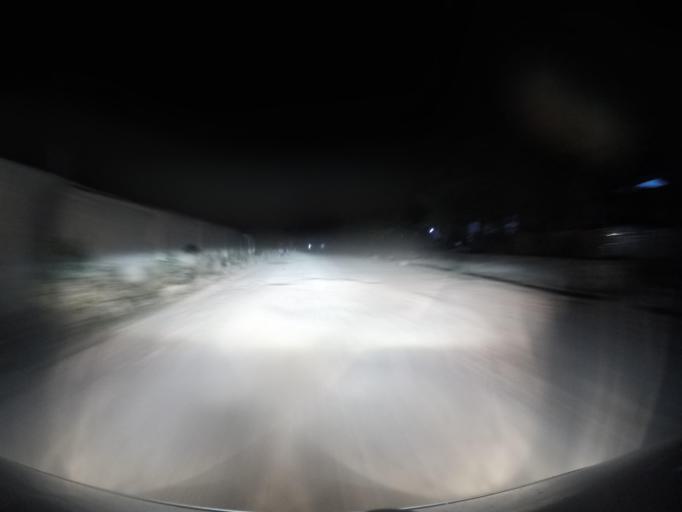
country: TL
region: Viqueque
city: Viqueque
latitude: -8.8026
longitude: 126.5500
